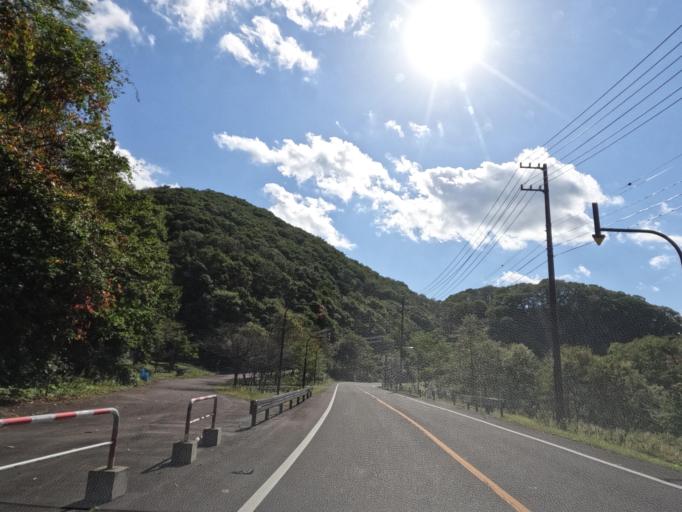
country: JP
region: Hokkaido
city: Shiraoi
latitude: 42.4840
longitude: 141.1453
